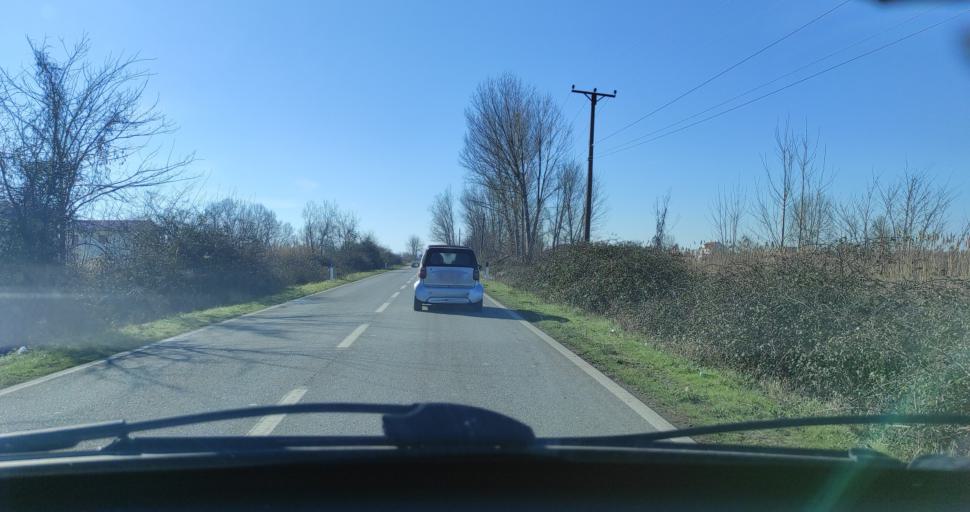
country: AL
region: Shkoder
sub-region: Rrethi i Shkodres
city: Velipoje
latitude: 41.8977
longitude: 19.4030
